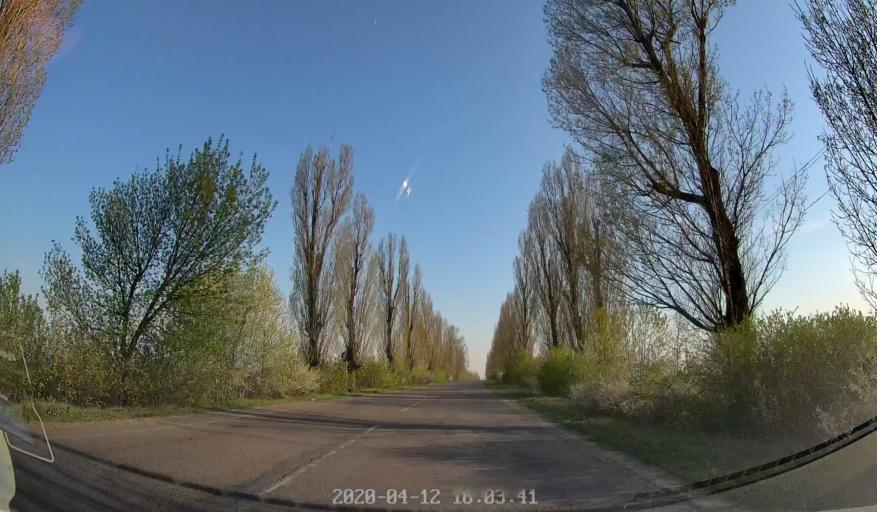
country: MD
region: Telenesti
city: Cocieri
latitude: 47.3814
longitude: 29.0432
